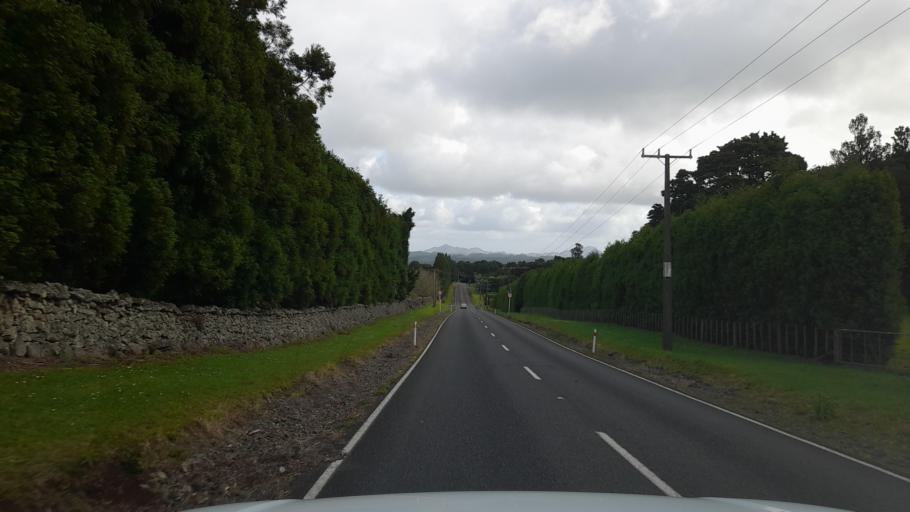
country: NZ
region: Northland
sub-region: Whangarei
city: Maungatapere
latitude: -35.7485
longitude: 174.2538
